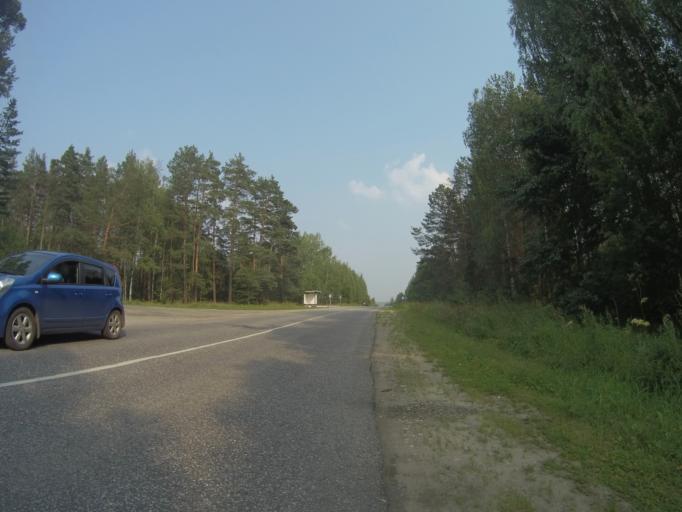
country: RU
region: Vladimir
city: Vorsha
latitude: 56.0117
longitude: 40.1449
